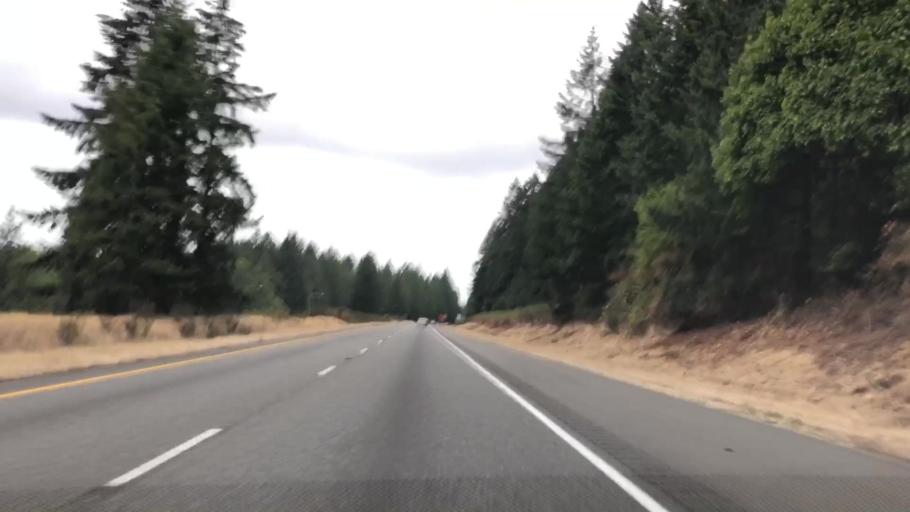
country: US
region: Washington
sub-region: Kitsap County
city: Burley
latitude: 47.4209
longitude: -122.6228
